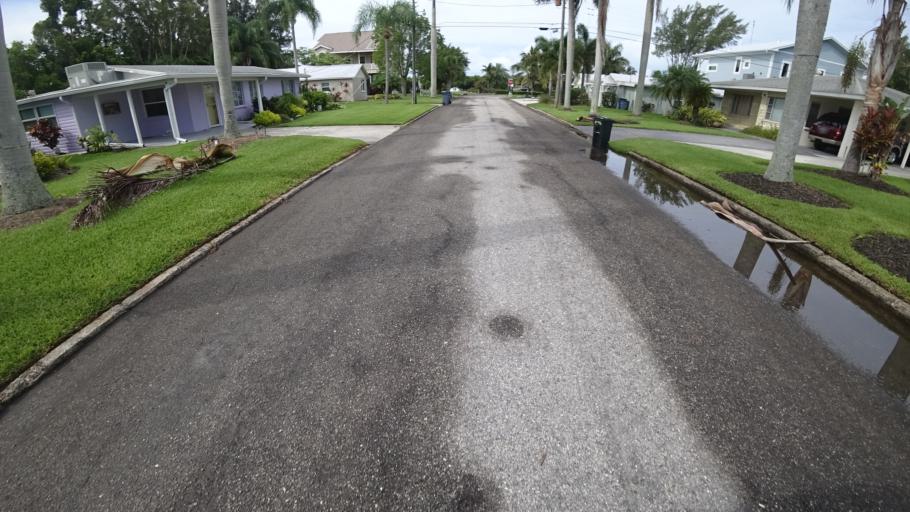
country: US
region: Florida
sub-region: Manatee County
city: Cortez
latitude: 27.4590
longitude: -82.6669
